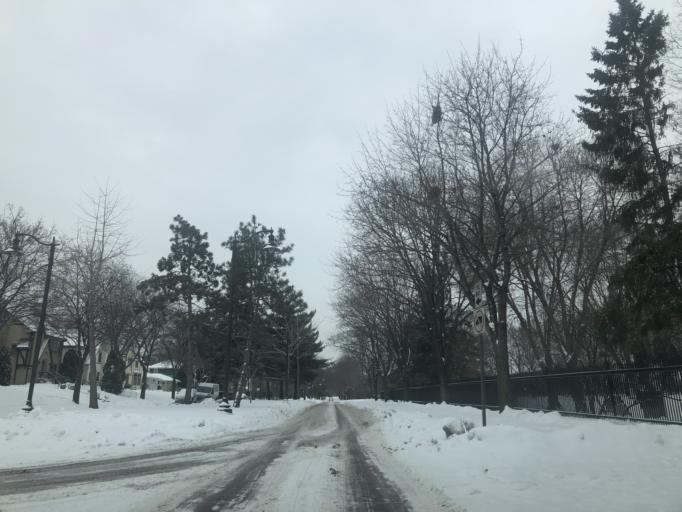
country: US
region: Minnesota
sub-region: Hennepin County
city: Richfield
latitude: 44.9305
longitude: -93.2936
